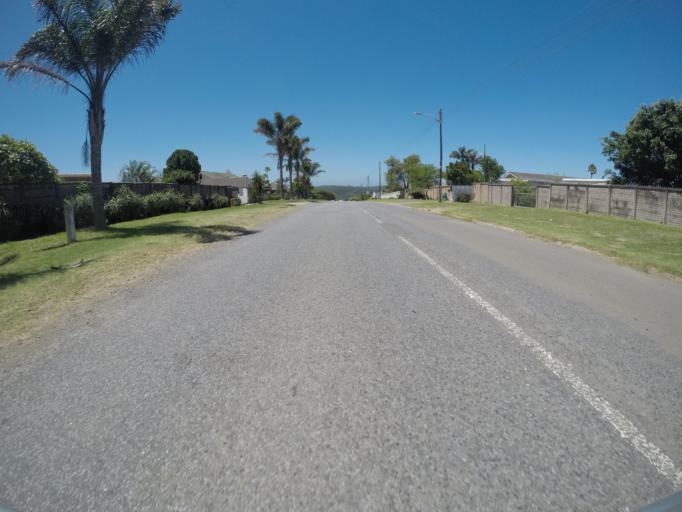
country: ZA
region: Eastern Cape
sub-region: Buffalo City Metropolitan Municipality
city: East London
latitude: -32.9568
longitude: 27.9406
